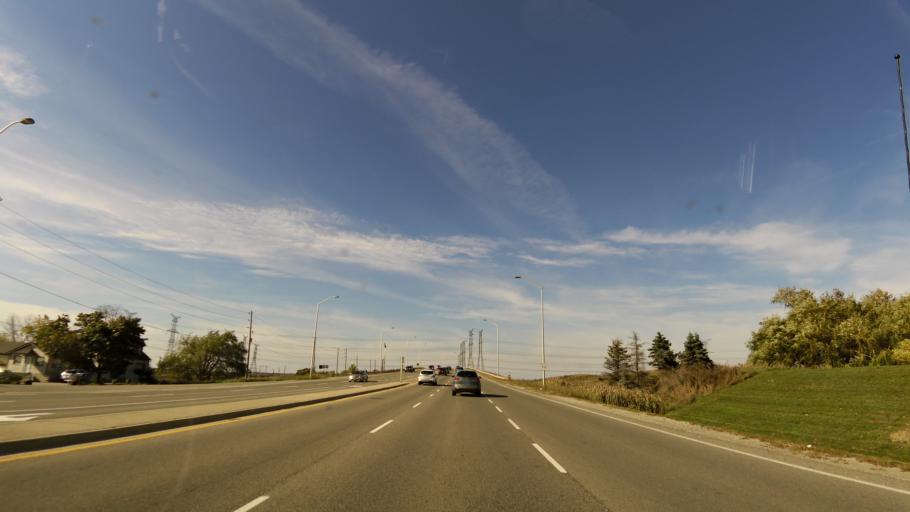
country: CA
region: Ontario
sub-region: Halton
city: Milton
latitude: 43.5611
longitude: -79.8156
